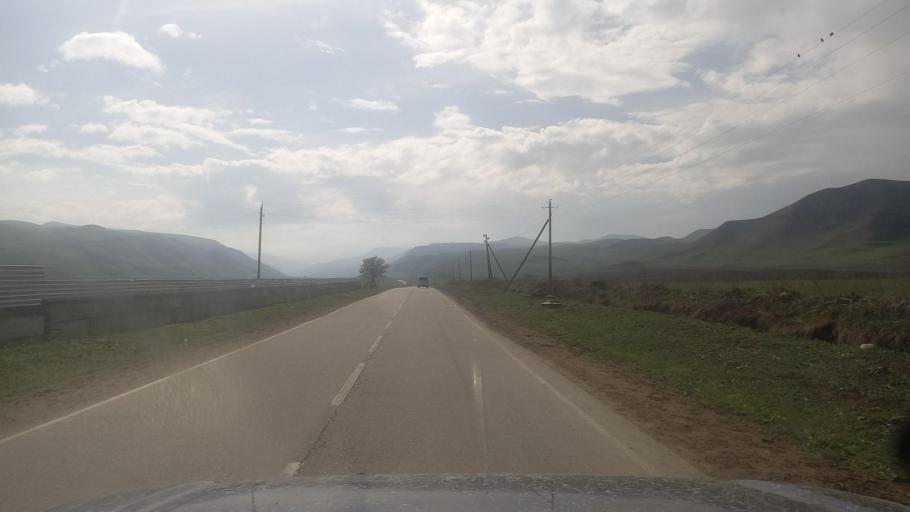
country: RU
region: Kabardino-Balkariya
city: Kamennomostskoye
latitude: 43.7359
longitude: 43.0098
